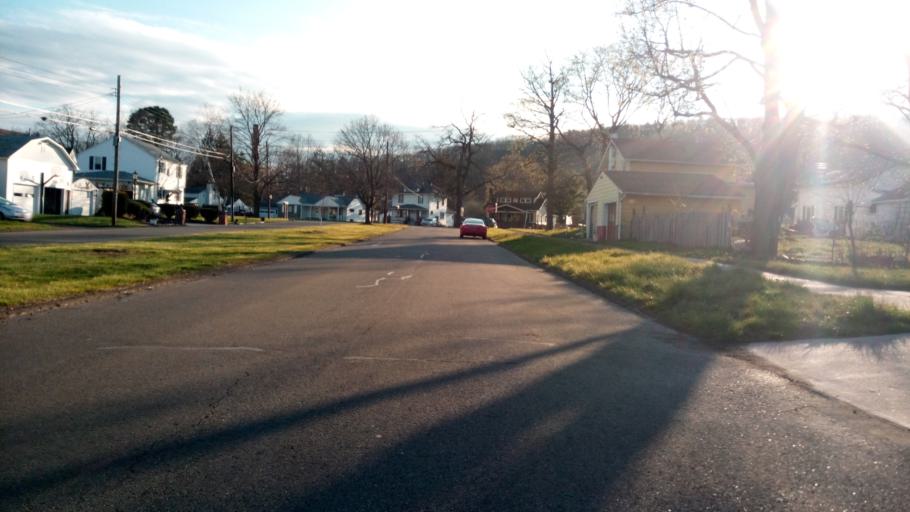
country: US
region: New York
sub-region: Chemung County
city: Elmira Heights
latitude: 42.1188
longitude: -76.8264
